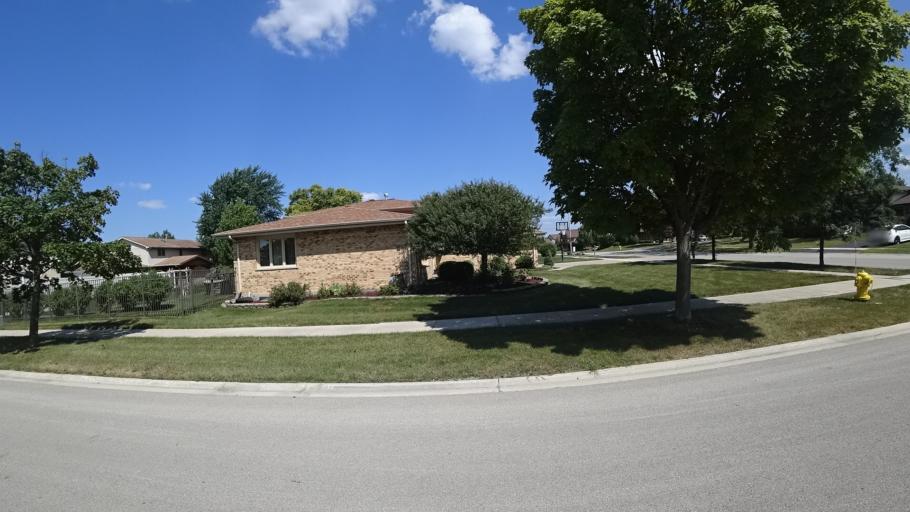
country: US
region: Illinois
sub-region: Cook County
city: Orland Park
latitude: 41.6358
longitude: -87.8471
